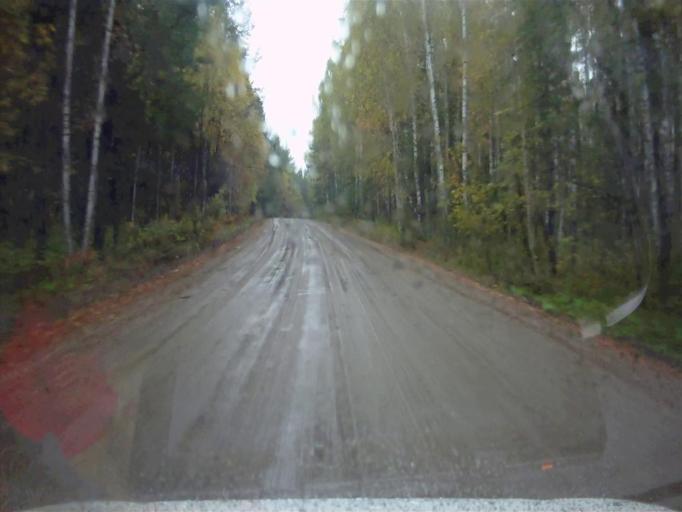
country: RU
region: Chelyabinsk
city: Kyshtym
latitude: 55.8861
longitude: 60.4654
